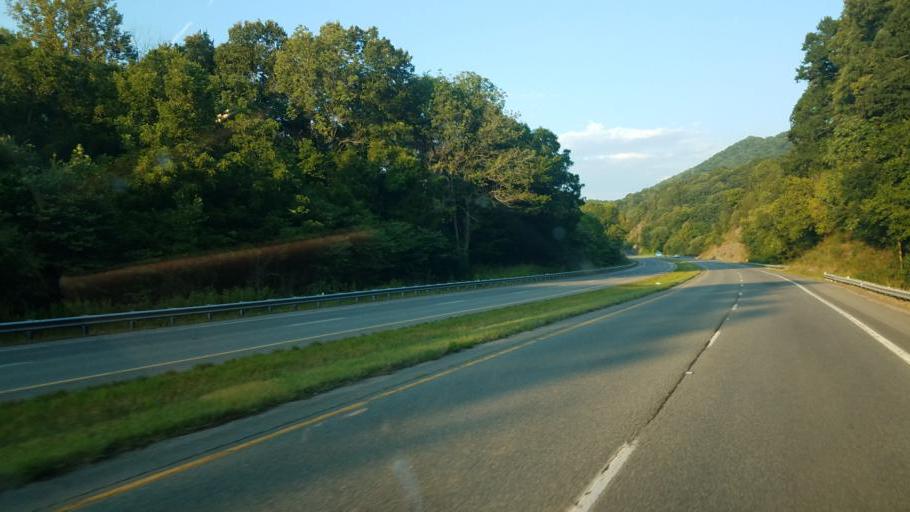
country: US
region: Virginia
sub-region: Scott County
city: Gate City
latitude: 36.6309
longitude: -82.5908
